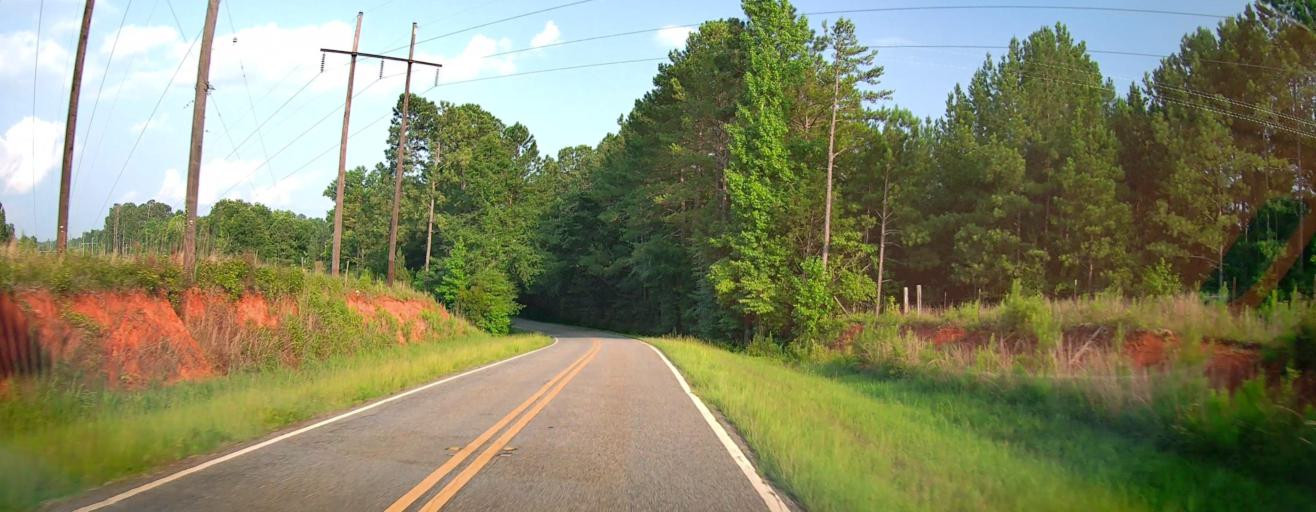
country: US
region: Georgia
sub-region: Monroe County
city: Forsyth
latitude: 33.0975
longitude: -83.7632
